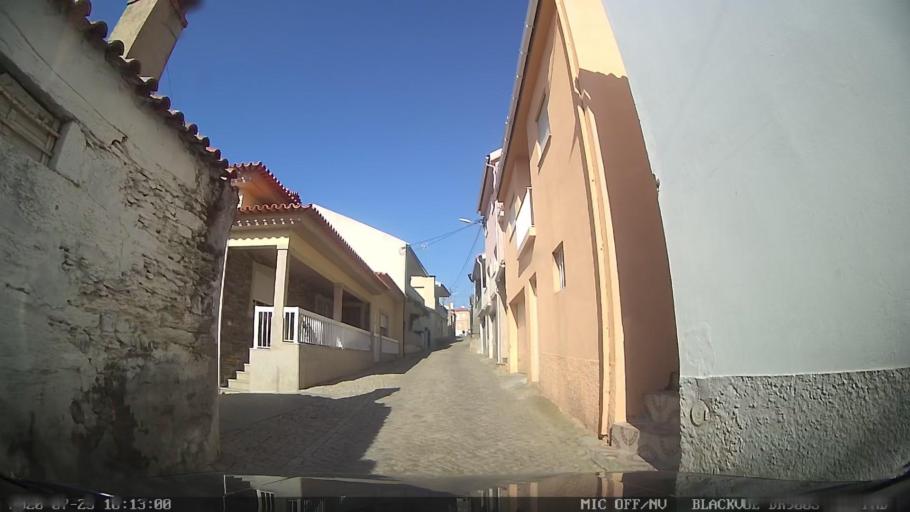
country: PT
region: Viseu
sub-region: Sao Joao da Pesqueira
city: Sao Joao da Pesqueira
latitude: 41.1873
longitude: -7.4310
